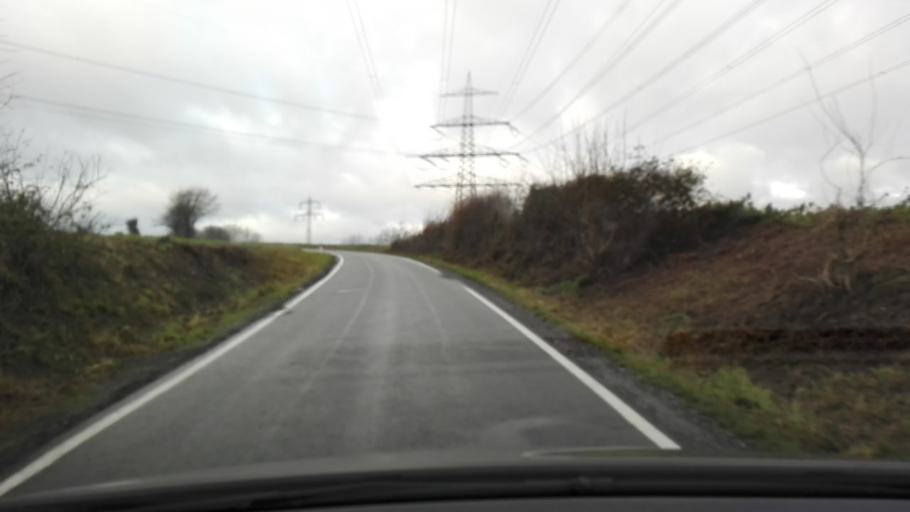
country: DE
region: North Rhine-Westphalia
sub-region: Regierungsbezirk Arnsberg
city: Frondenberg
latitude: 51.5174
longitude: 7.7386
